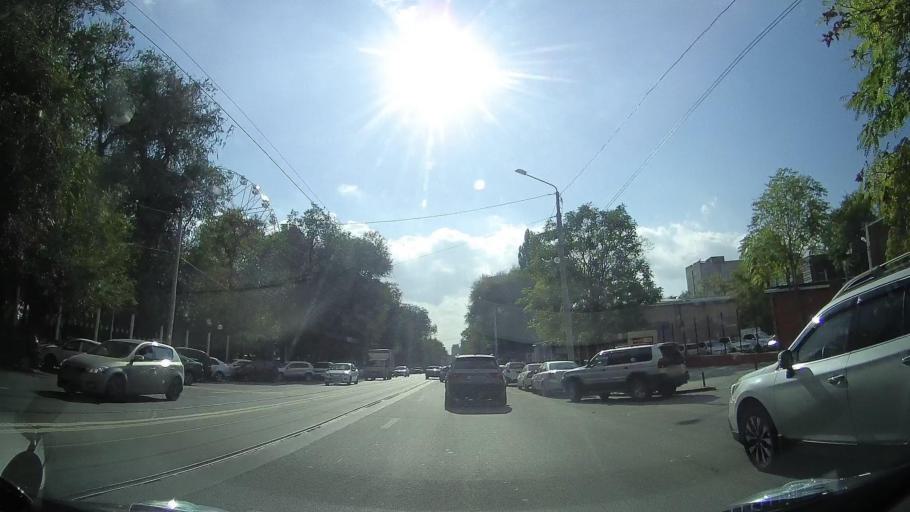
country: RU
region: Rostov
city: Rostov-na-Donu
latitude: 47.2302
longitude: 39.7413
